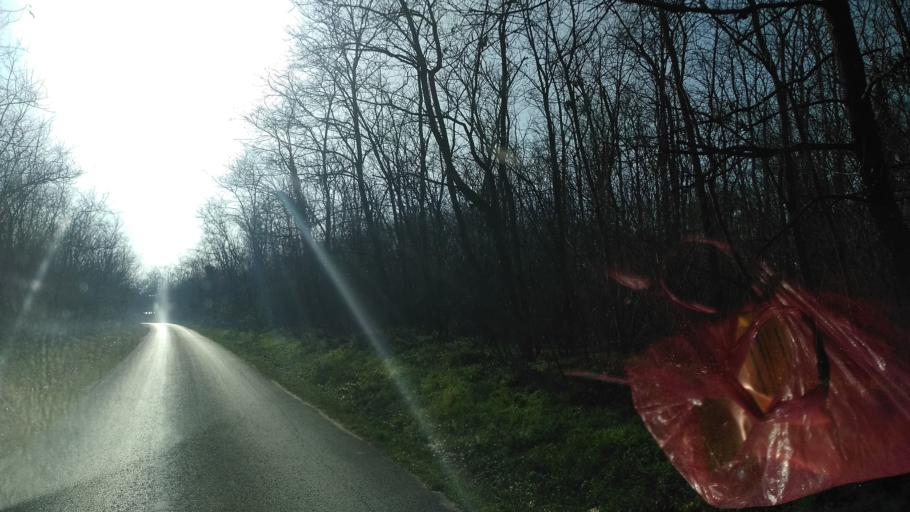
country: HU
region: Somogy
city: Barcs
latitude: 45.9561
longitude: 17.5078
